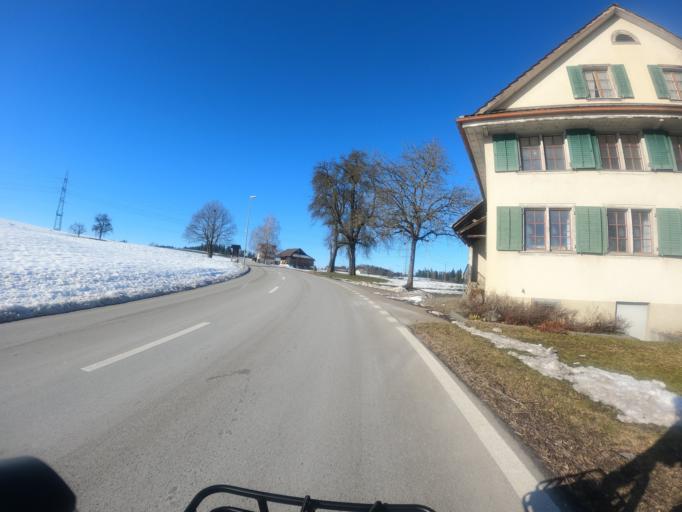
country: CH
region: Zurich
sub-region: Bezirk Affoltern
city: Hedingen
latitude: 47.2887
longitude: 8.4290
